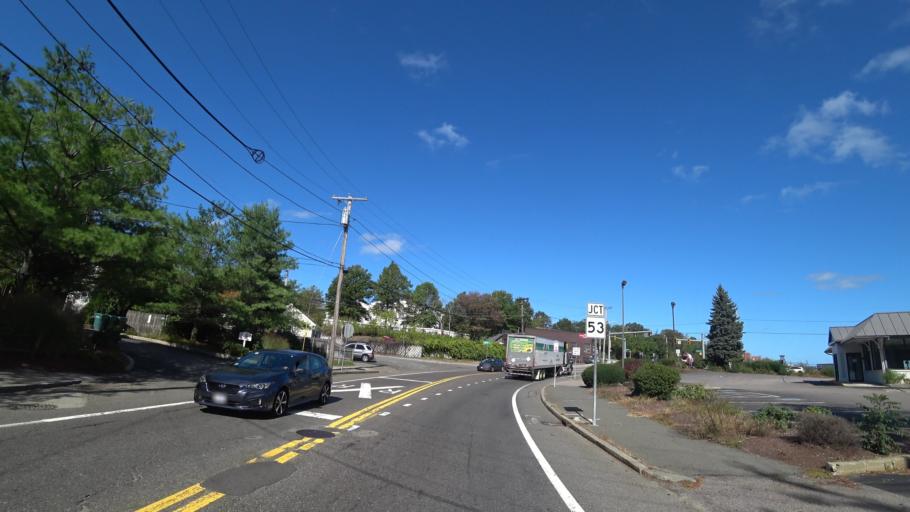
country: US
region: Massachusetts
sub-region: Norfolk County
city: Braintree
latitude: 42.2360
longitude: -70.9812
